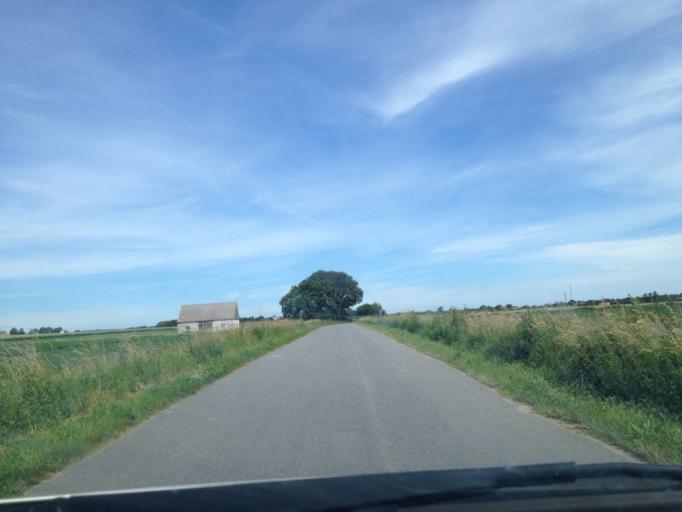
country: DK
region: Central Jutland
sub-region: Samso Kommune
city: Tranebjerg
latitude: 55.9418
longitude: 10.5565
